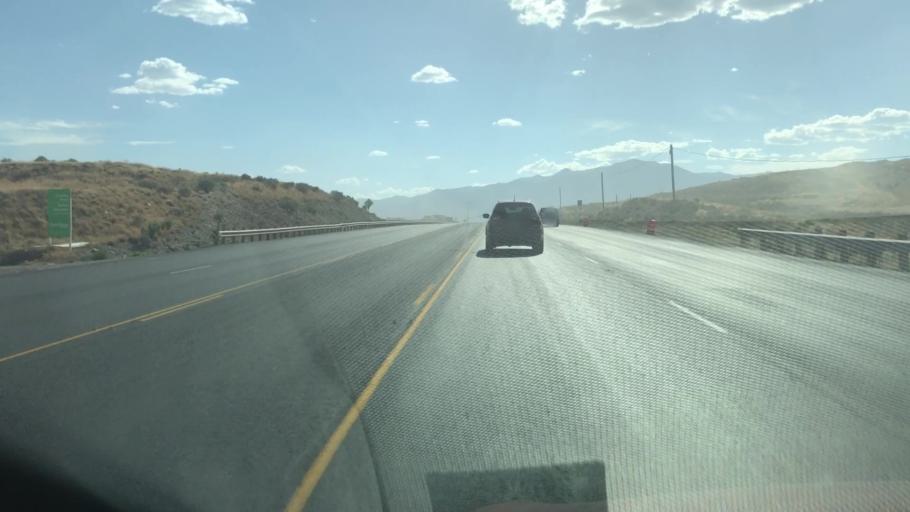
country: US
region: Utah
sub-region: Utah County
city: Saratoga Springs
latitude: 40.3830
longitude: -111.9573
